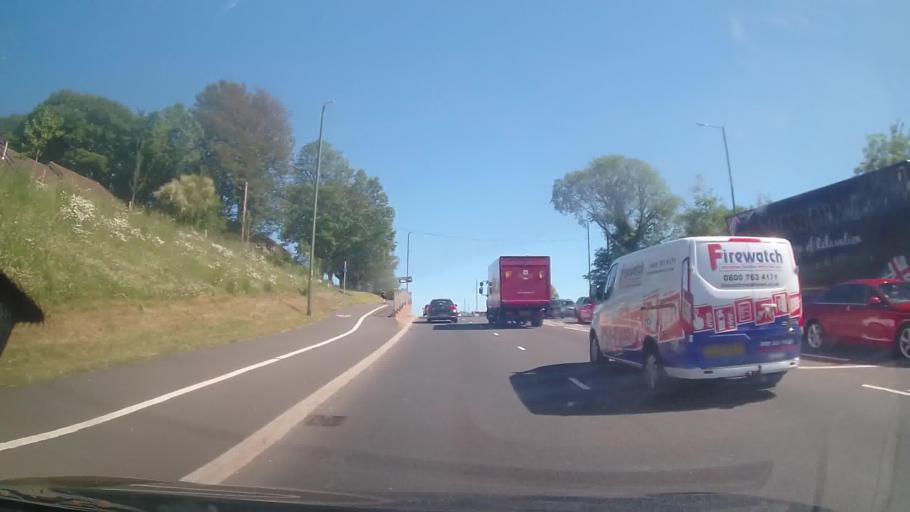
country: GB
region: England
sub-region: Borough of Torbay
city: Paignton
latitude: 50.4212
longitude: -3.5871
